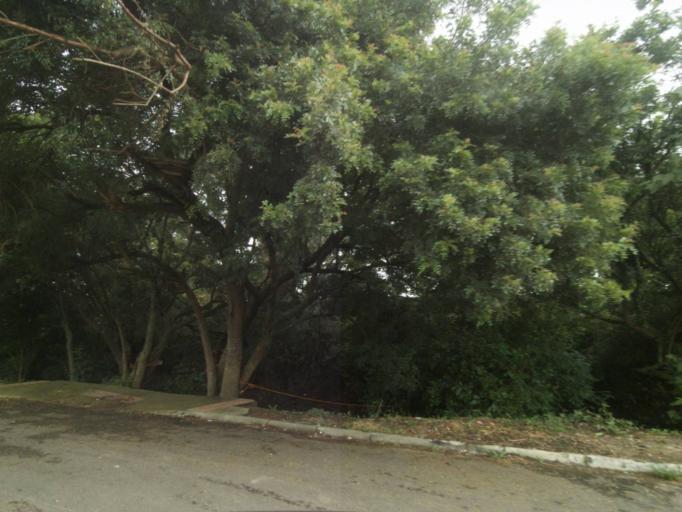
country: BR
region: Parana
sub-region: Pinhais
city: Pinhais
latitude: -25.4627
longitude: -49.1925
